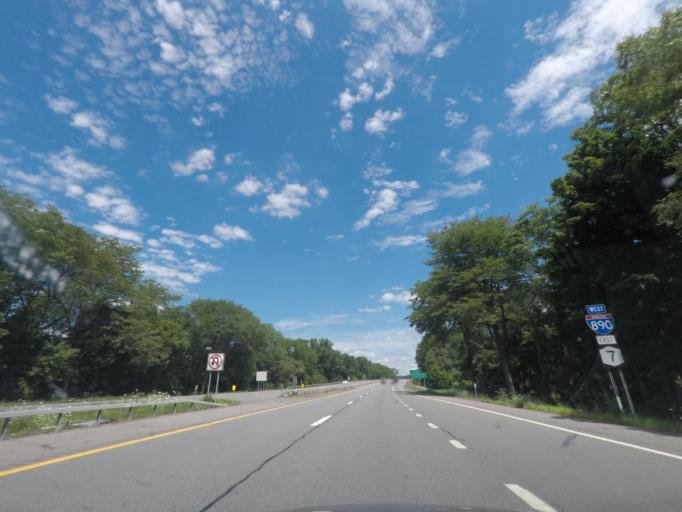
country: US
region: New York
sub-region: Schenectady County
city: Schenectady
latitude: 42.7753
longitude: -73.9256
